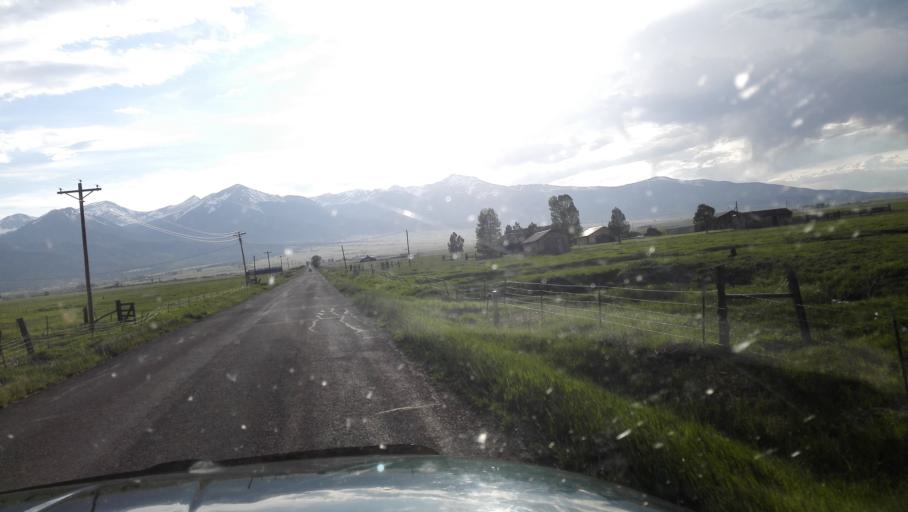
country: US
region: Colorado
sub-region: Custer County
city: Westcliffe
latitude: 38.1316
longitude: -105.4888
